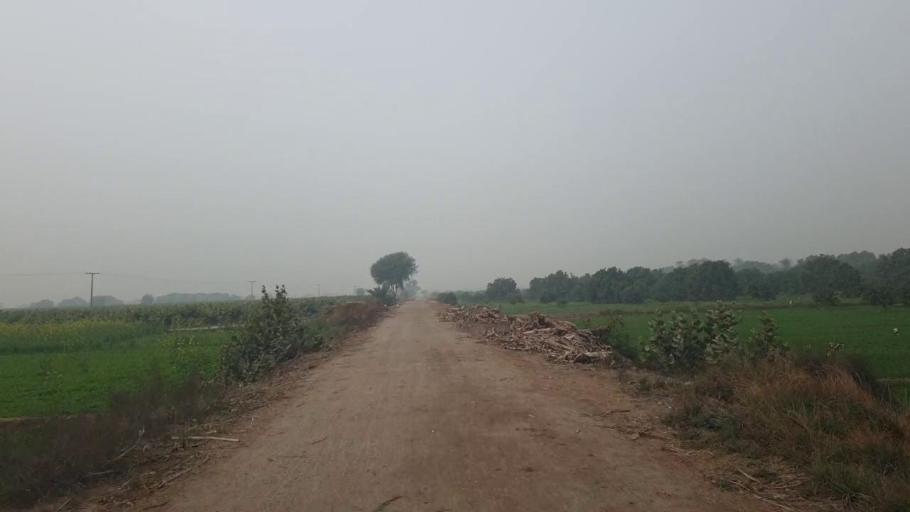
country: PK
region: Sindh
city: Tando Adam
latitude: 25.7215
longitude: 68.6370
